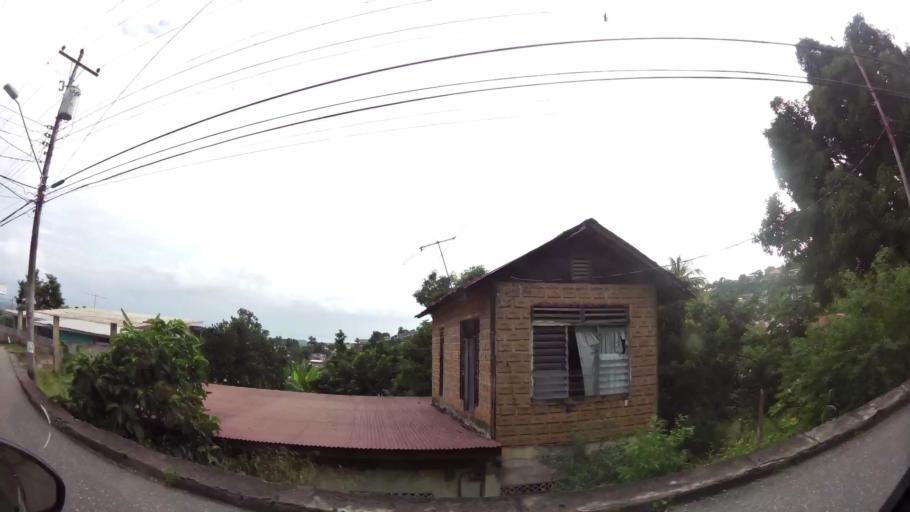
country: TT
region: San Juan/Laventille
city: Laventille
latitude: 10.6619
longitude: -61.4863
